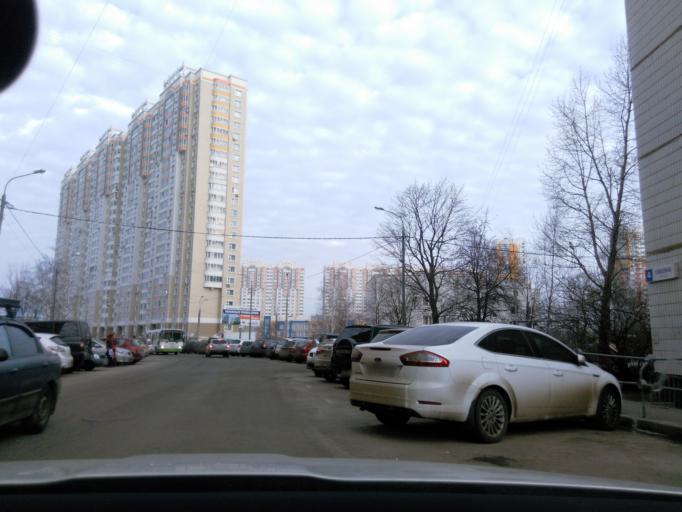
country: RU
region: Moskovskaya
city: Levoberezhnaya
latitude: 55.8975
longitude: 37.4801
